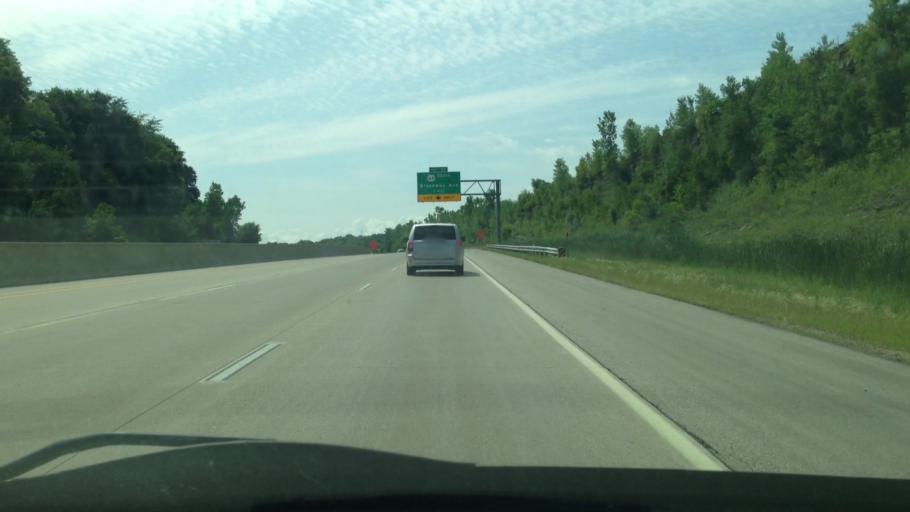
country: US
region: Minnesota
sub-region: Olmsted County
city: Rochester
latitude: 43.9883
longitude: -92.4795
